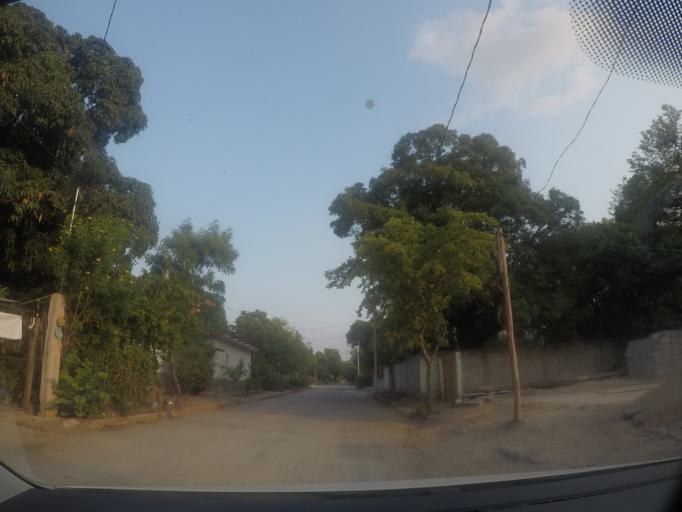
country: MX
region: Oaxaca
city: San Jeronimo Ixtepec
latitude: 16.5860
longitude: -95.2101
